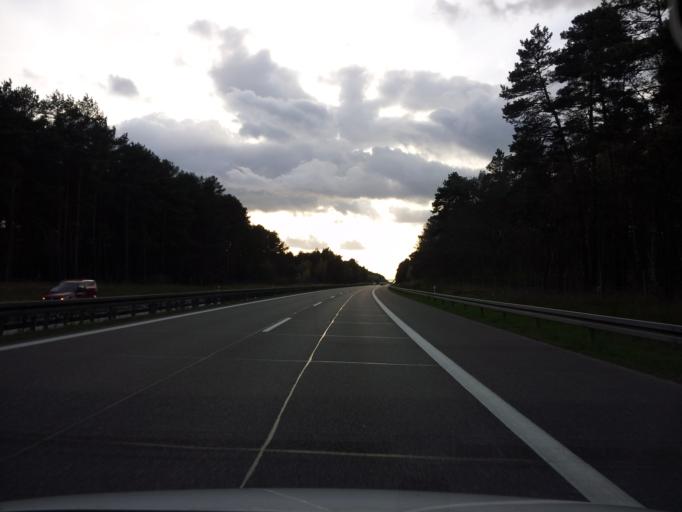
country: DE
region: Brandenburg
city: Kolkwitz
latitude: 51.7226
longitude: 14.2676
